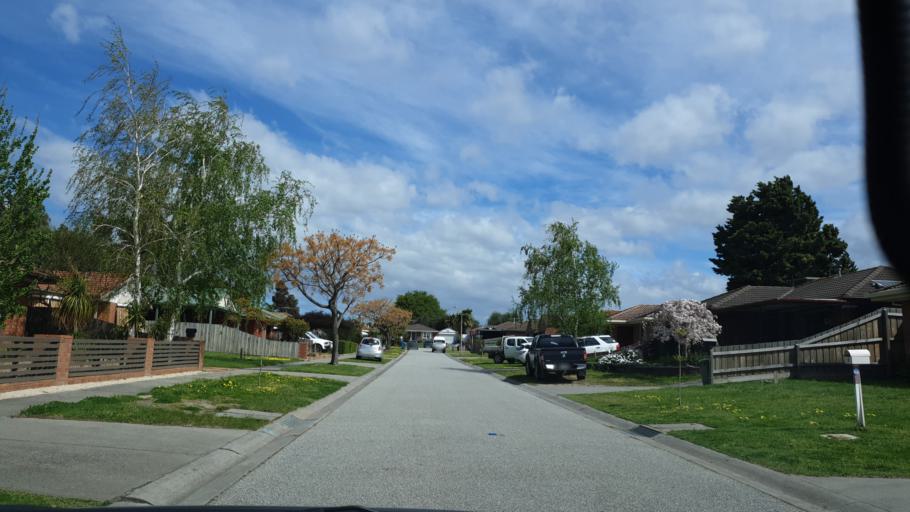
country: AU
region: Victoria
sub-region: Casey
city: Cranbourne North
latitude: -38.0798
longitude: 145.2956
